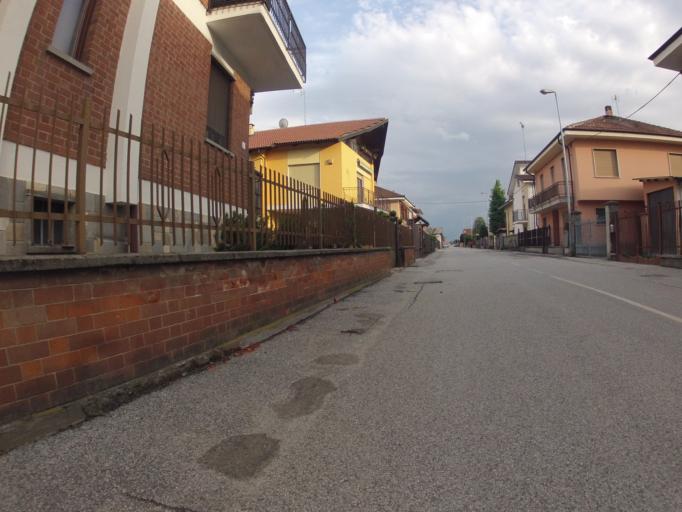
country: IT
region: Piedmont
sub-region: Provincia di Cuneo
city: Moretta
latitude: 44.7600
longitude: 7.5386
